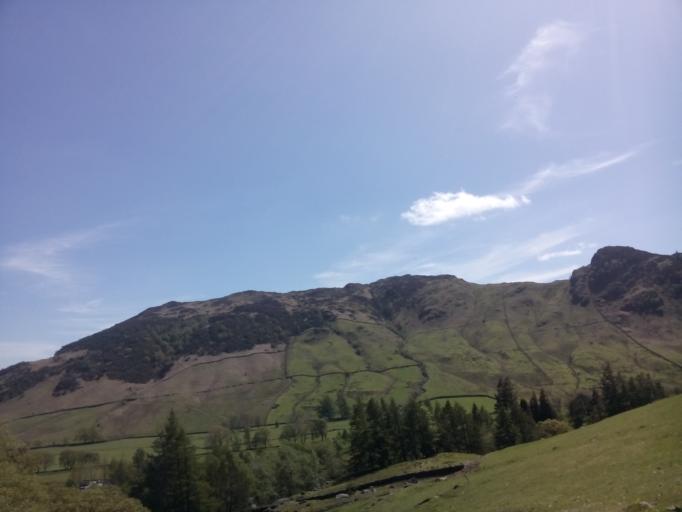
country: GB
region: England
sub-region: Cumbria
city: Ambleside
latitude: 54.4500
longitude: -3.0920
